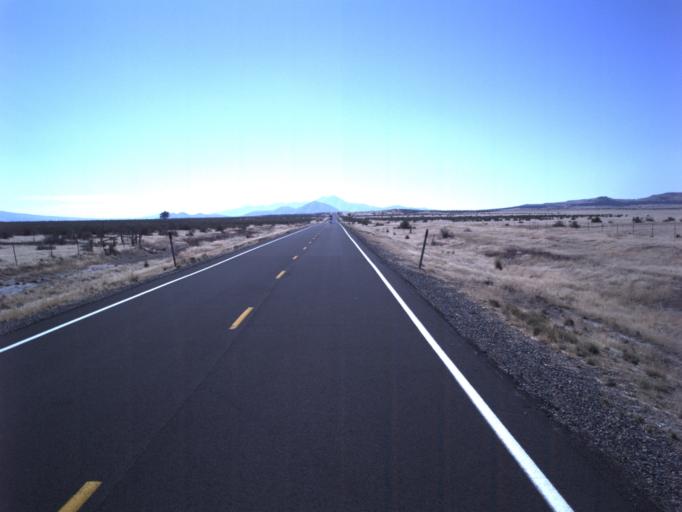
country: US
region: Utah
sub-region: Tooele County
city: Grantsville
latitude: 40.3106
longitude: -112.7433
